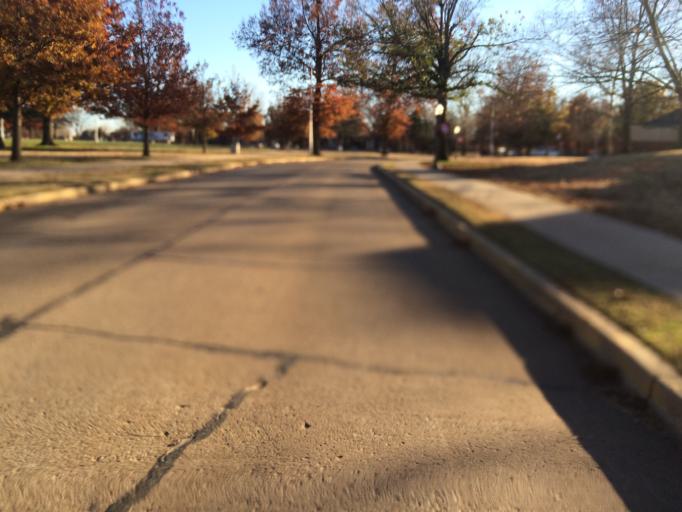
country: US
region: Oklahoma
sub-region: Cleveland County
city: Norman
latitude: 35.1963
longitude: -97.4443
